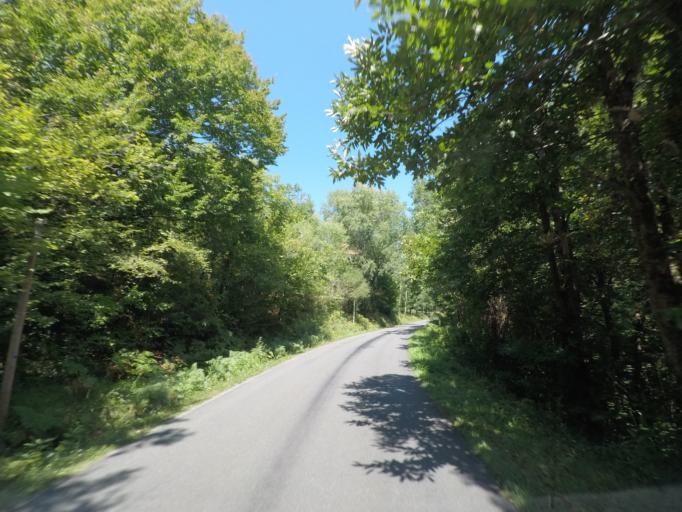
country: FR
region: Midi-Pyrenees
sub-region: Departement de l'Aveyron
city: Livinhac-le-Haut
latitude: 44.6054
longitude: 2.2286
